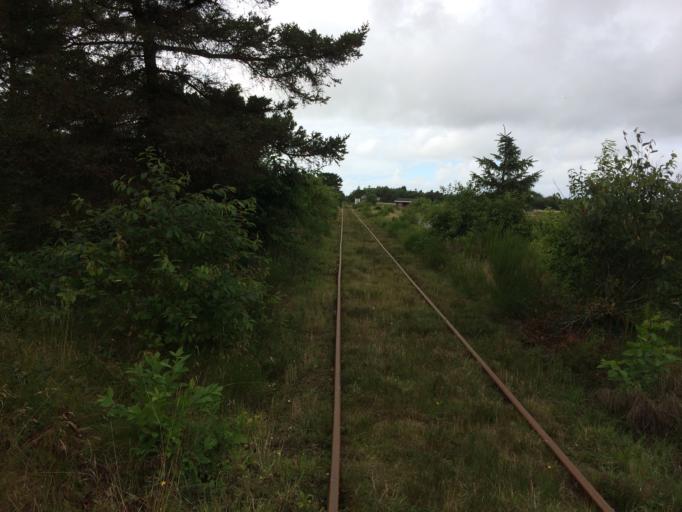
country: DK
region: South Denmark
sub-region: Varde Kommune
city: Oksbol
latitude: 55.8079
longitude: 8.2118
